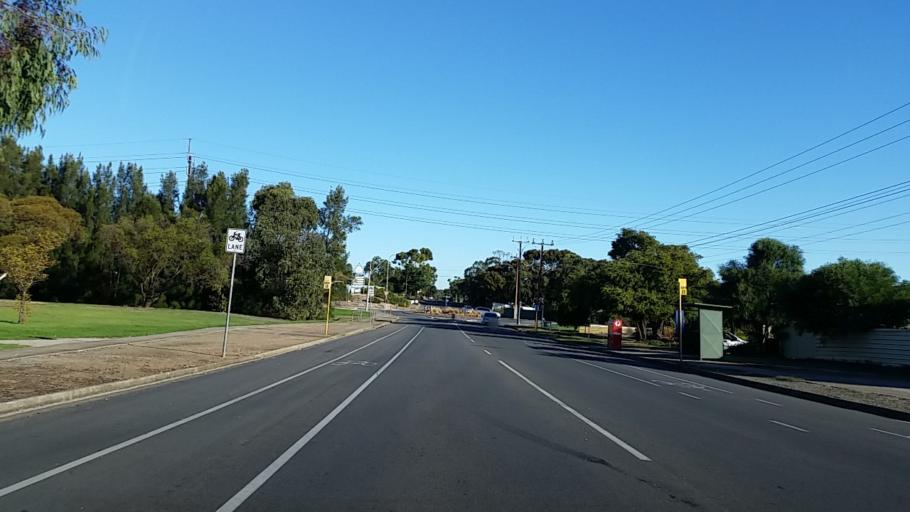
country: AU
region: South Australia
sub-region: Onkaparinga
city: Reynella
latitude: -35.1140
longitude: 138.5355
